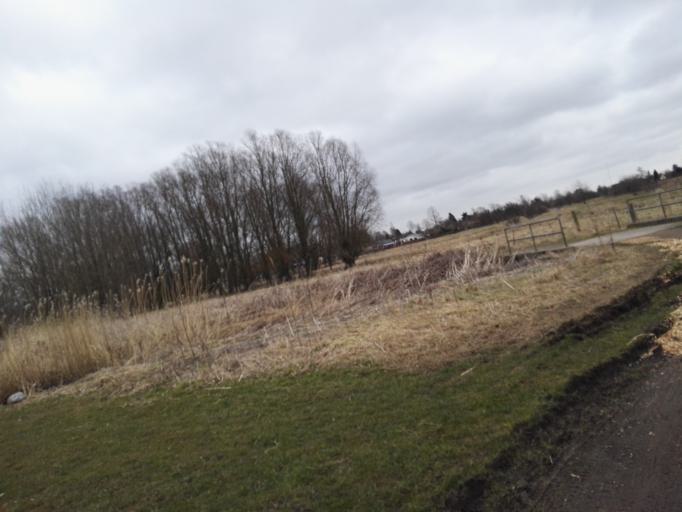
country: DK
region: Capital Region
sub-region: Ballerup Kommune
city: Ballerup
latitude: 55.7106
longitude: 12.3719
